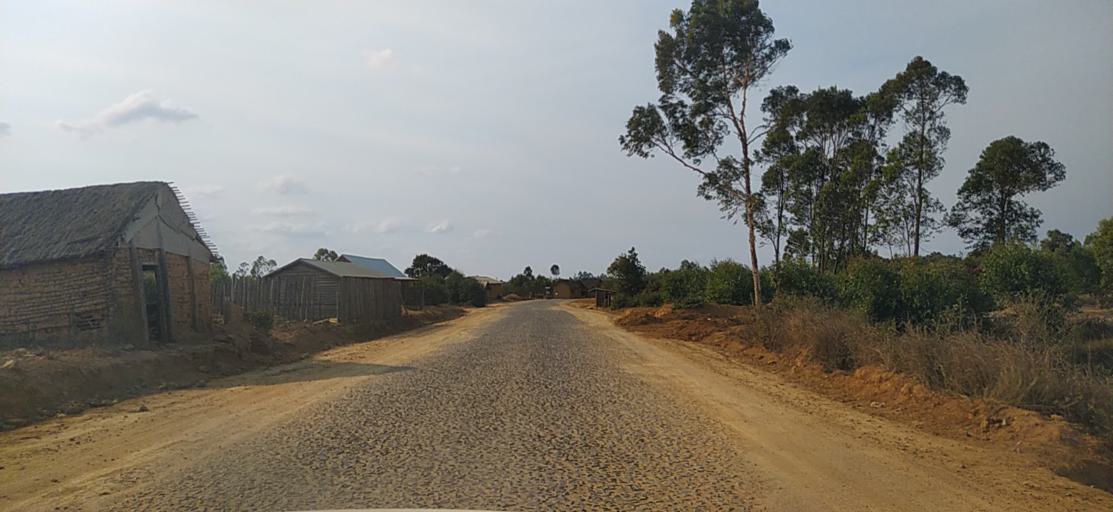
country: MG
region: Alaotra Mangoro
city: Moramanga
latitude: -18.6642
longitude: 48.2740
